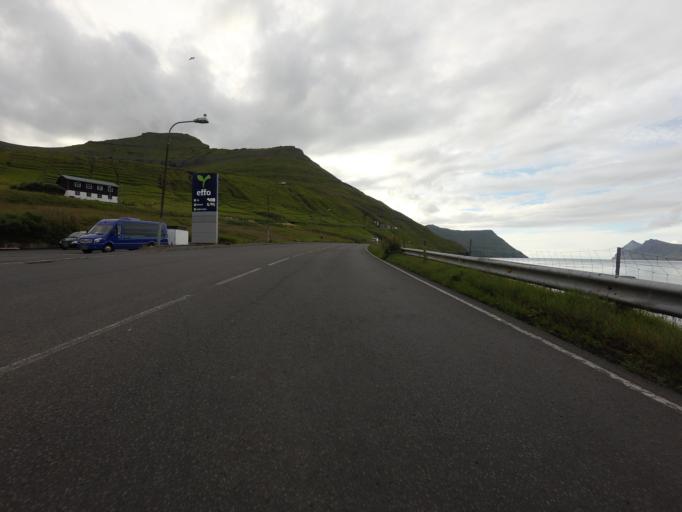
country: FO
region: Eysturoy
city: Eystur
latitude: 62.2134
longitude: -6.7141
